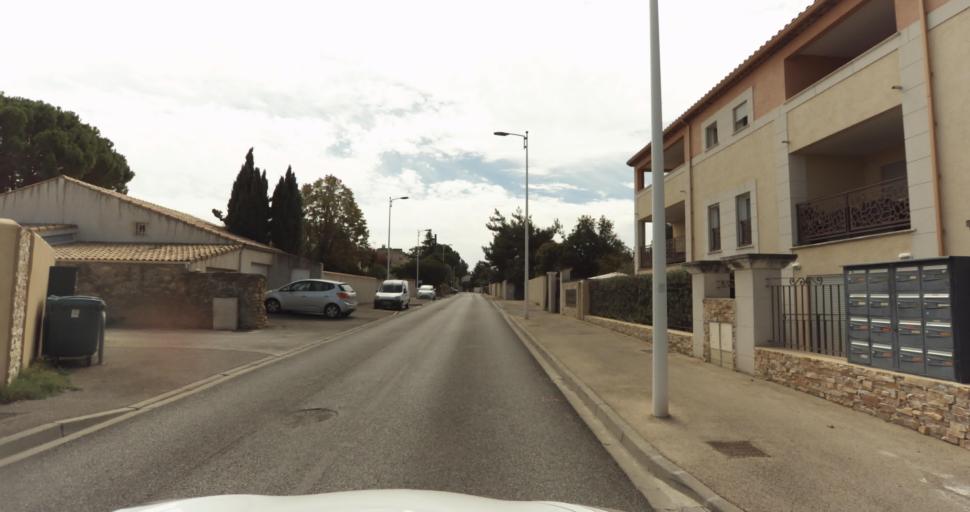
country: FR
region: Provence-Alpes-Cote d'Azur
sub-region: Departement des Bouches-du-Rhone
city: Miramas
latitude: 43.5850
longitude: 5.0133
